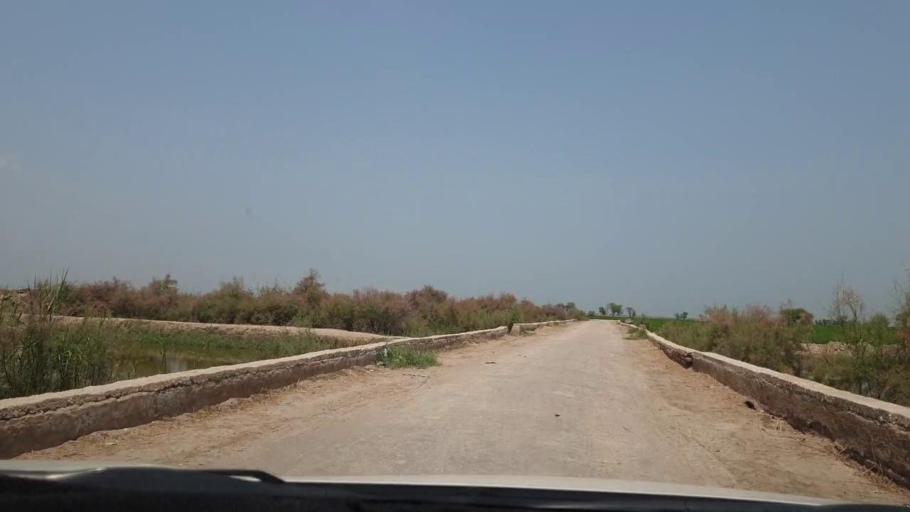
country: PK
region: Sindh
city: Radhan
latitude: 27.2428
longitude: 68.0005
